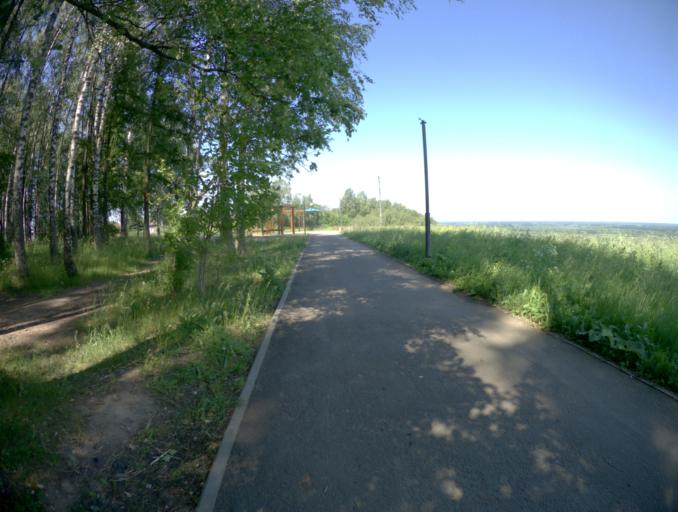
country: RU
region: Vladimir
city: Vyazniki
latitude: 56.2377
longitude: 42.1947
